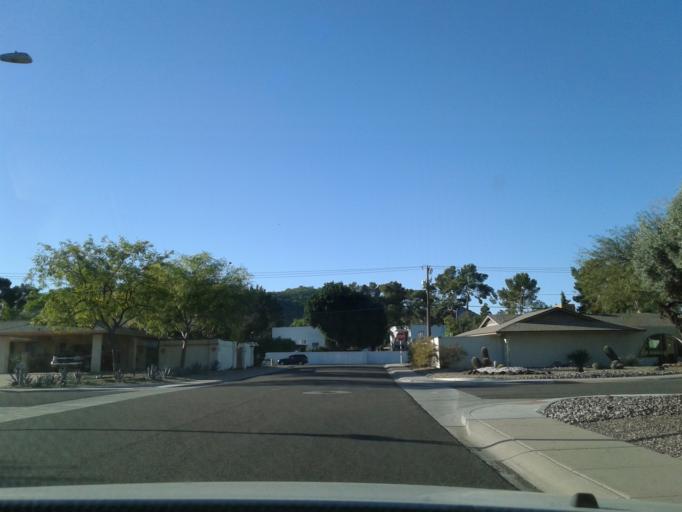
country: US
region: Arizona
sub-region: Maricopa County
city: Glendale
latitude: 33.6085
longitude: -112.0689
